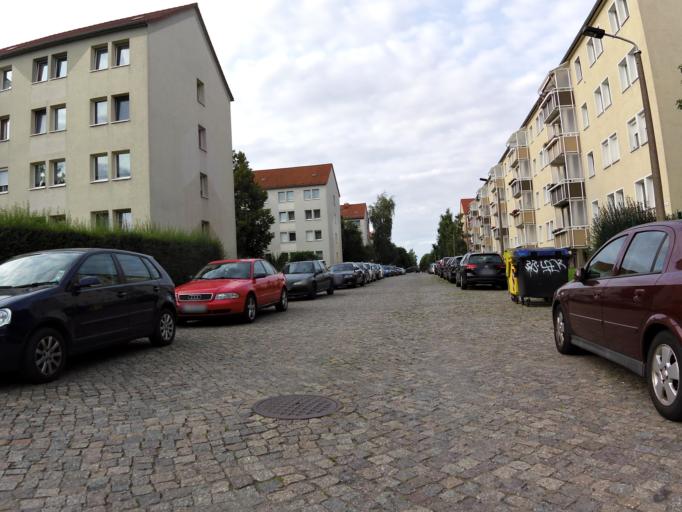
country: DE
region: Saxony
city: Leipzig
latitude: 51.3750
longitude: 12.4007
